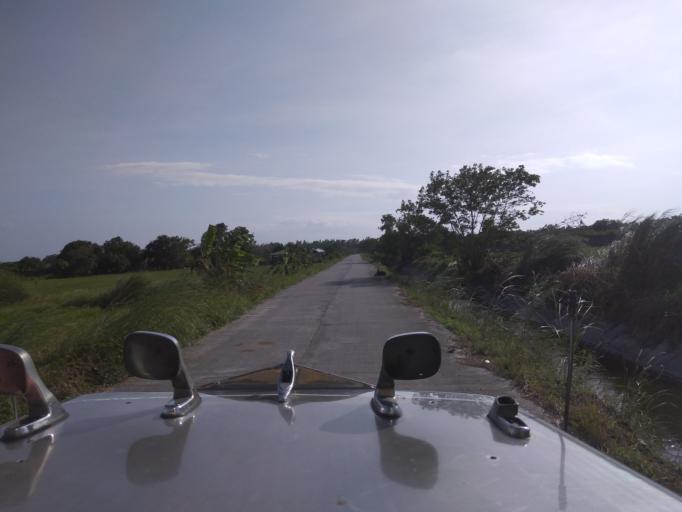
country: PH
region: Central Luzon
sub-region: Province of Pampanga
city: San Patricio
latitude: 15.0983
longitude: 120.6982
